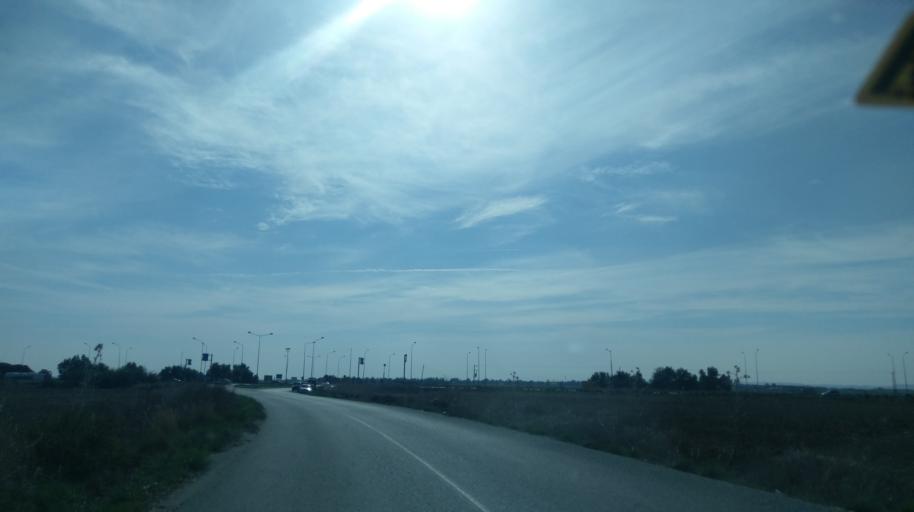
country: CY
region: Ammochostos
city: Lefkonoiko
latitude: 35.1848
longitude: 33.7001
